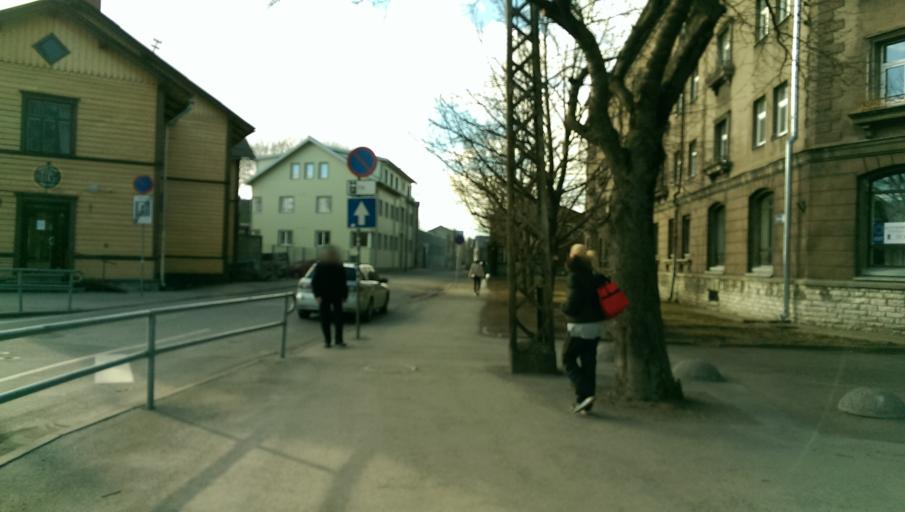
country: EE
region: Harju
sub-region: Tallinna linn
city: Tallinn
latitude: 59.4419
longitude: 24.7351
